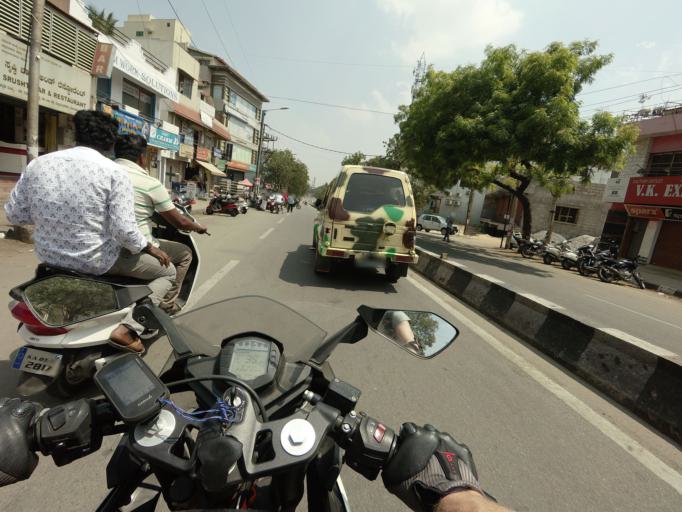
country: IN
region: Karnataka
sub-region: Bangalore Urban
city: Bangalore
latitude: 13.0098
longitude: 77.6432
